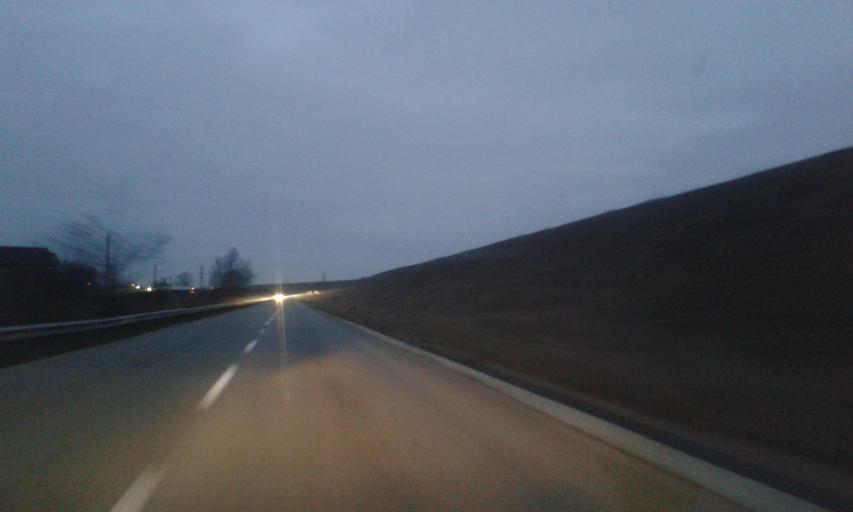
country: RO
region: Gorj
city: Targu Jiu
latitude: 45.0639
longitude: 23.2756
